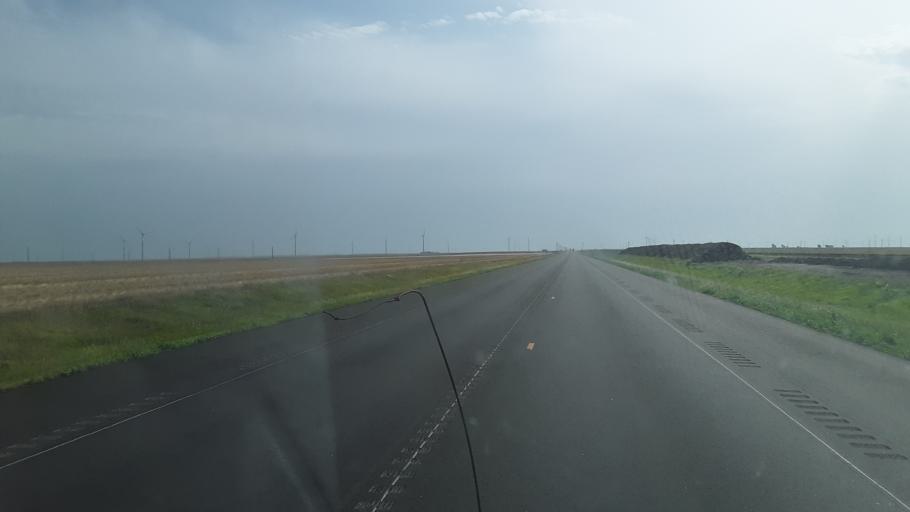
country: US
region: Kansas
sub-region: Ford County
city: Dodge City
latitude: 37.7893
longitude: -99.8791
